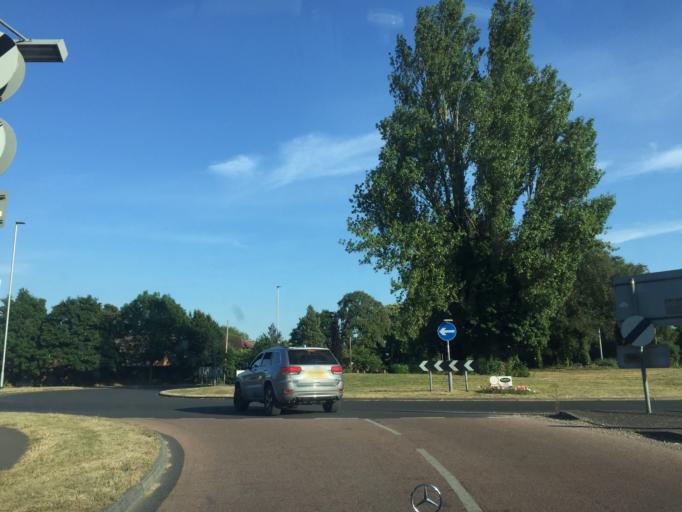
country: GB
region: England
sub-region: Wokingham
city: Wargrave
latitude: 51.4871
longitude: -0.8704
